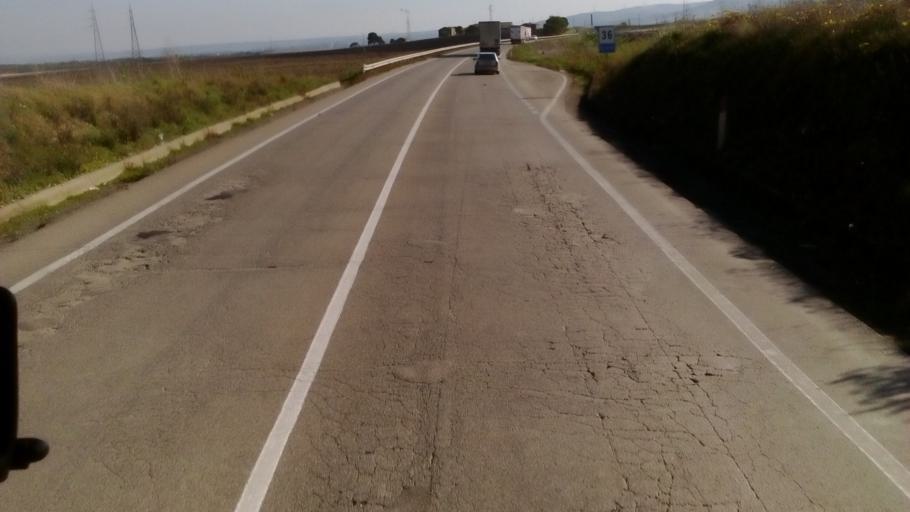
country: IT
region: Apulia
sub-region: Provincia di Foggia
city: Candela
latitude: 41.1182
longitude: 15.5761
